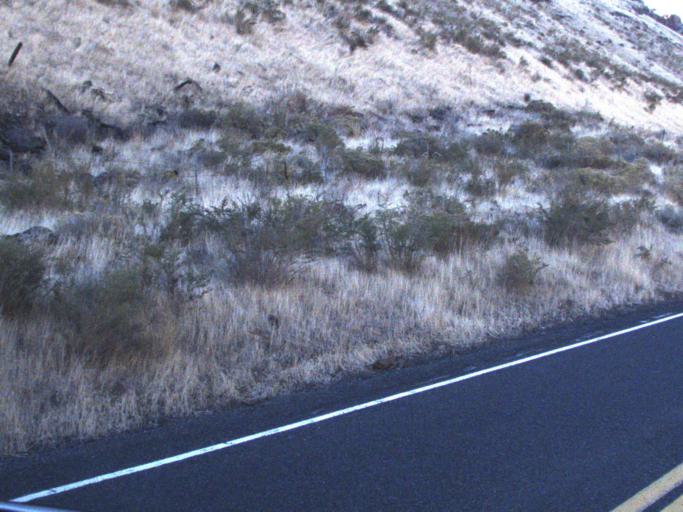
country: US
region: Washington
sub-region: Franklin County
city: Connell
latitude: 46.6074
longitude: -118.5528
